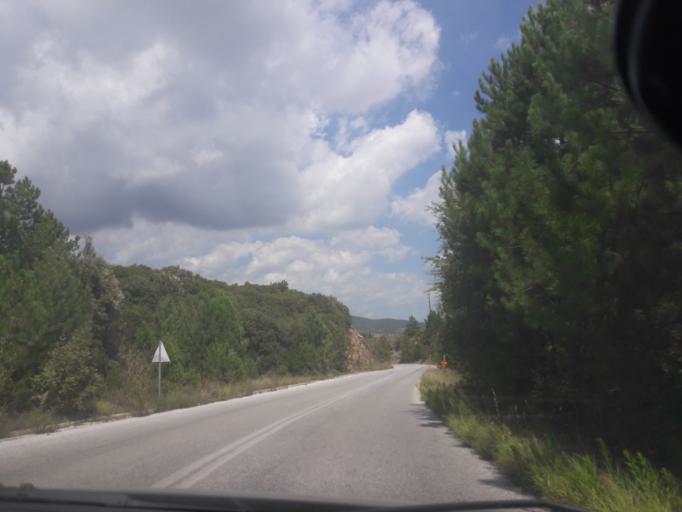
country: GR
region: Central Macedonia
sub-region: Nomos Chalkidikis
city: Polygyros
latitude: 40.3573
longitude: 23.4937
